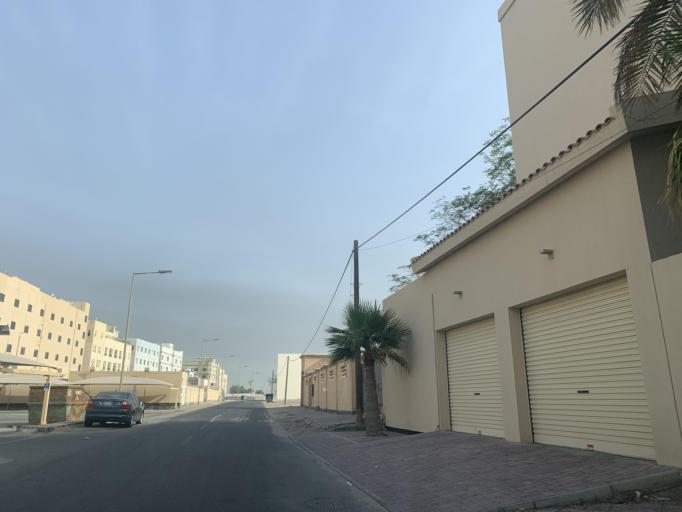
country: BH
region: Northern
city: Madinat `Isa
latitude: 26.1891
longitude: 50.5577
